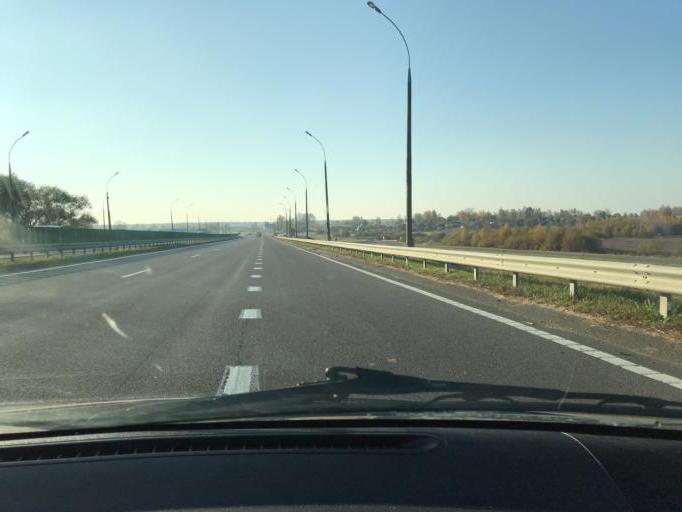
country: BY
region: Minsk
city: Loshnitsa
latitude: 54.2916
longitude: 28.7732
